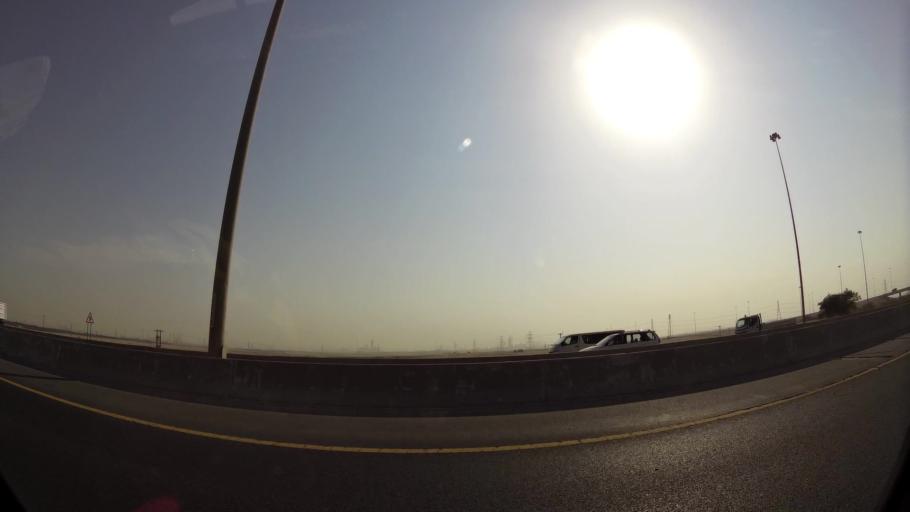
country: KW
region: Al Ahmadi
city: Al Ahmadi
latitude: 29.0386
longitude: 48.0931
